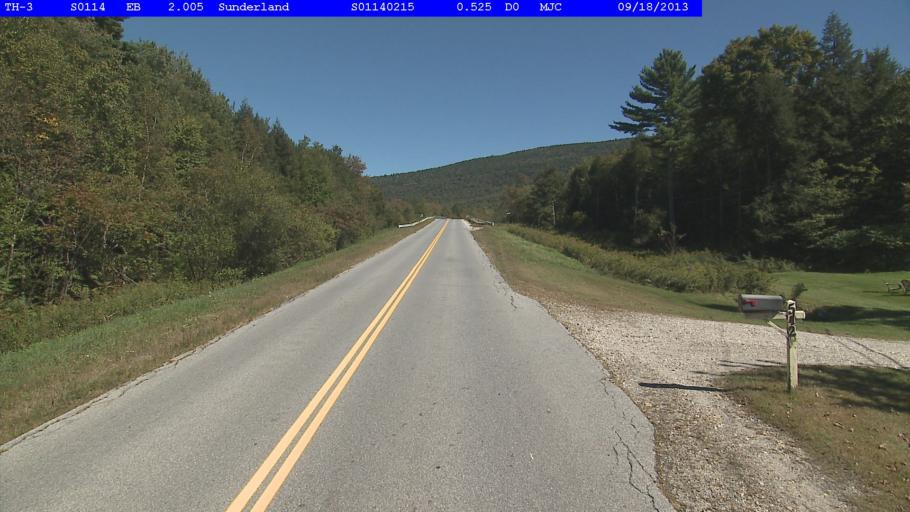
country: US
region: Vermont
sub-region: Bennington County
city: Arlington
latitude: 43.0581
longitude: -73.1283
